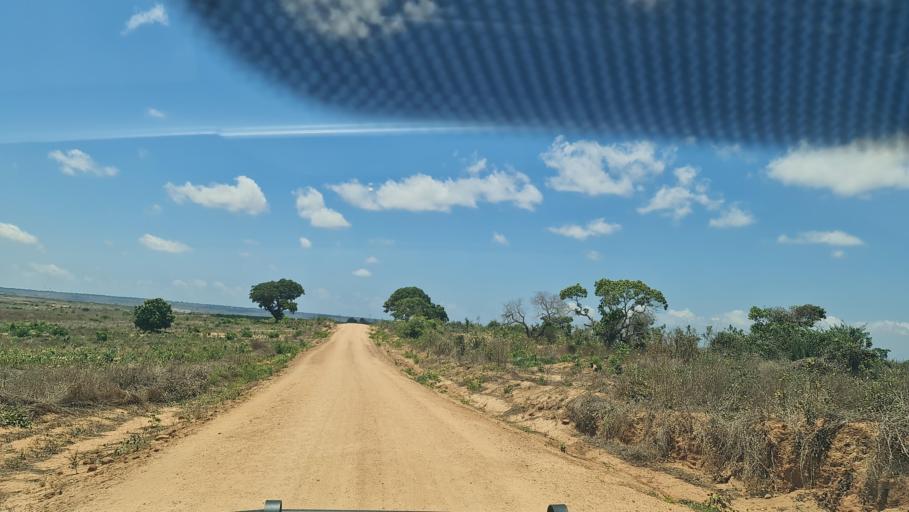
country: MZ
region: Nampula
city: Nacala
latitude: -14.3290
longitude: 40.5940
